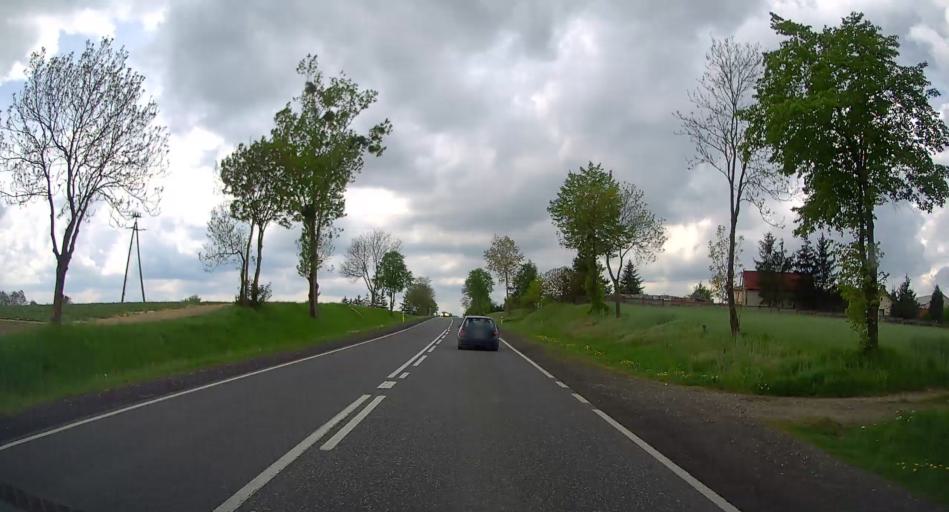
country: PL
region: Masovian Voivodeship
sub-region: Powiat plonski
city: Zaluski
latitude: 52.4327
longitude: 20.4643
